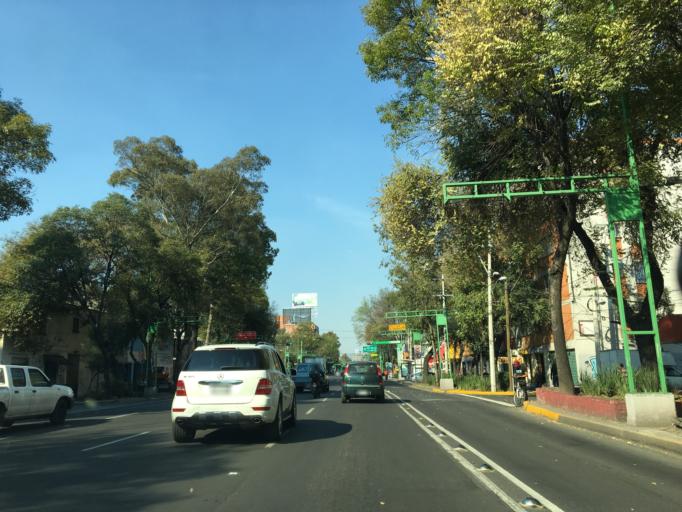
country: MX
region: Mexico City
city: Benito Juarez
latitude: 19.4089
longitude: -99.1444
